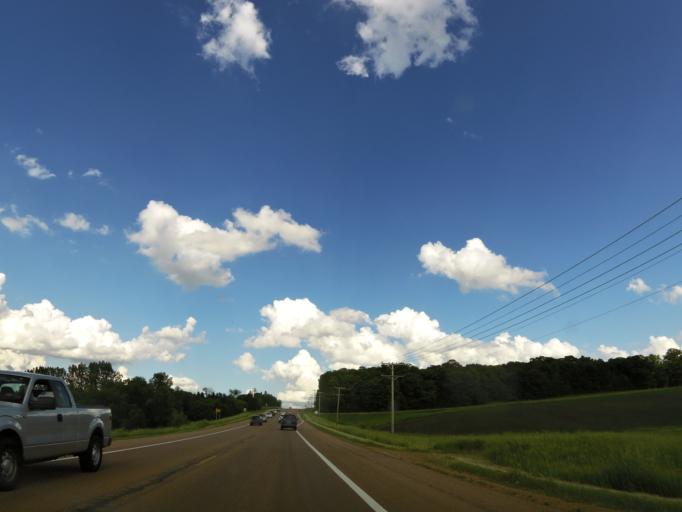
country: US
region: Minnesota
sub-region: Carver County
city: Victoria
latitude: 44.8189
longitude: -93.7218
